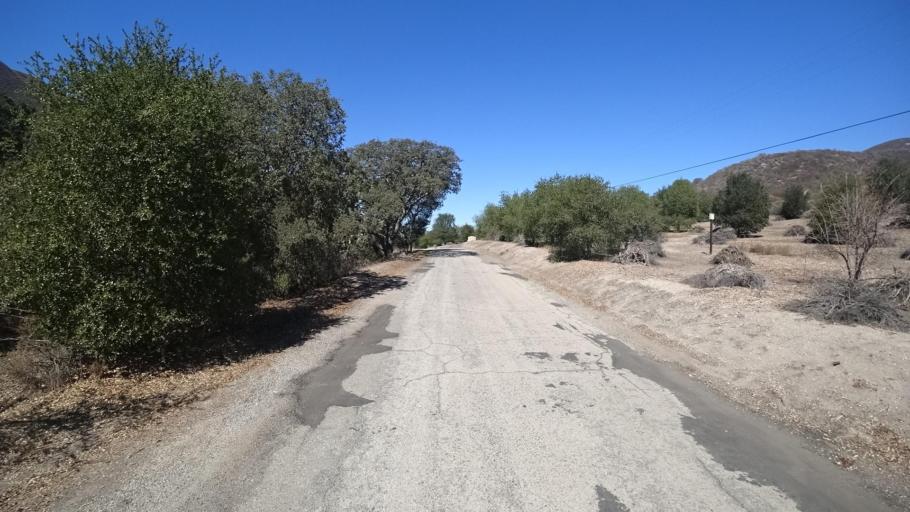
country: US
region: California
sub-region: Monterey County
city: Greenfield
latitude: 36.2665
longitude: -121.2977
